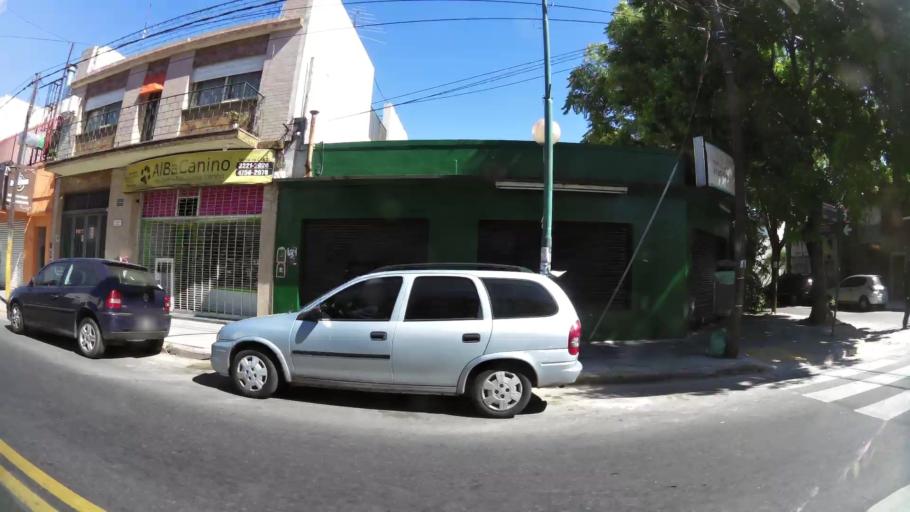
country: AR
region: Buenos Aires
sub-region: Partido de General San Martin
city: General San Martin
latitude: -34.5316
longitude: -58.5267
